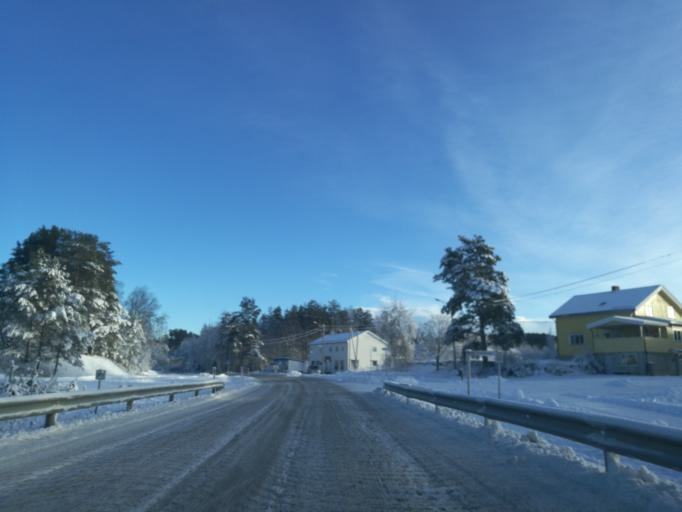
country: NO
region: Hedmark
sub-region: Grue
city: Kirkenaer
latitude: 60.4165
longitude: 12.3986
